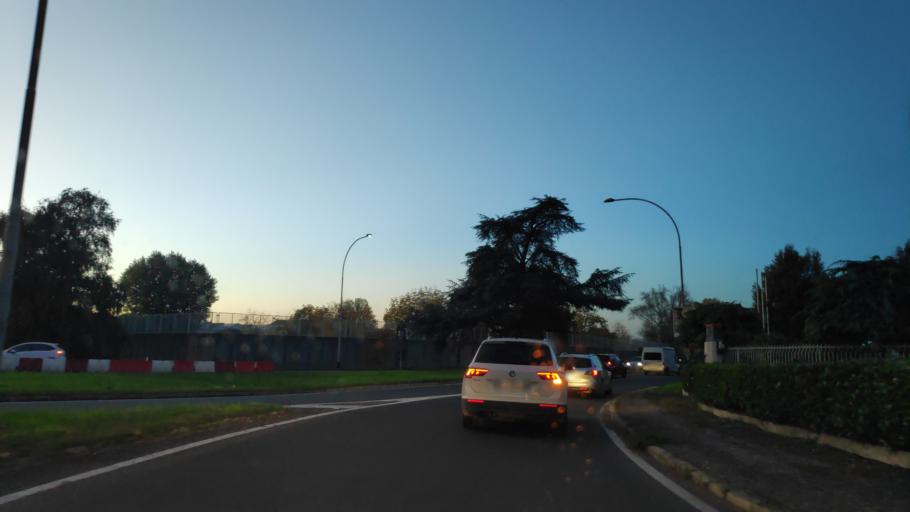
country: IT
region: Lombardy
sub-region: Citta metropolitana di Milano
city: Abbiategrasso
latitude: 45.3997
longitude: 8.9328
